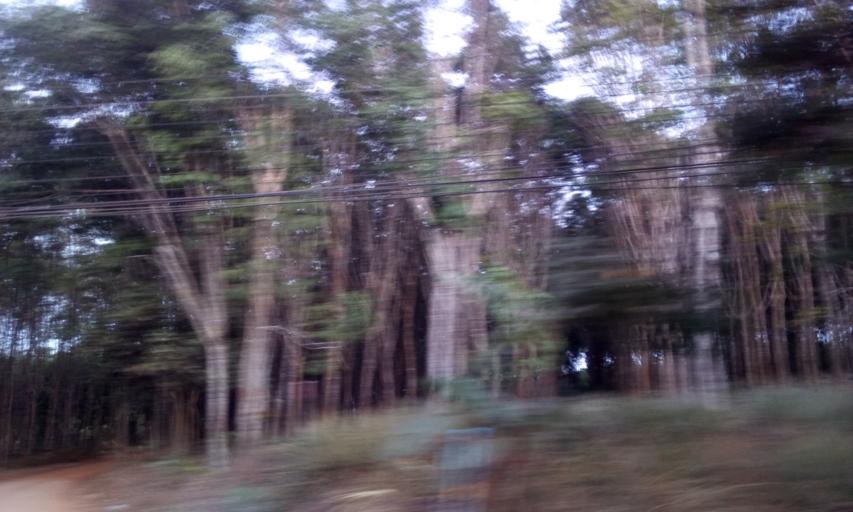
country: TH
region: Trat
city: Khao Saming
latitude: 12.3535
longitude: 102.3810
